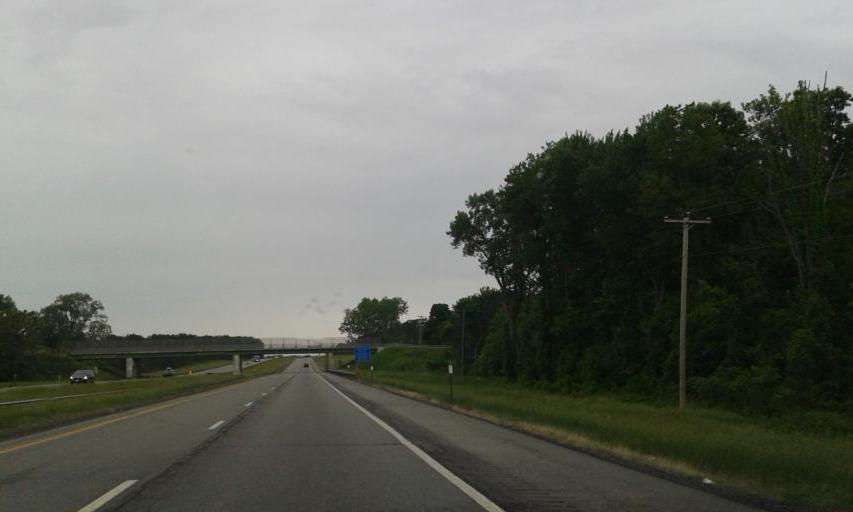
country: US
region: New York
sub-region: Livingston County
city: Caledonia
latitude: 43.0302
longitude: -77.8918
